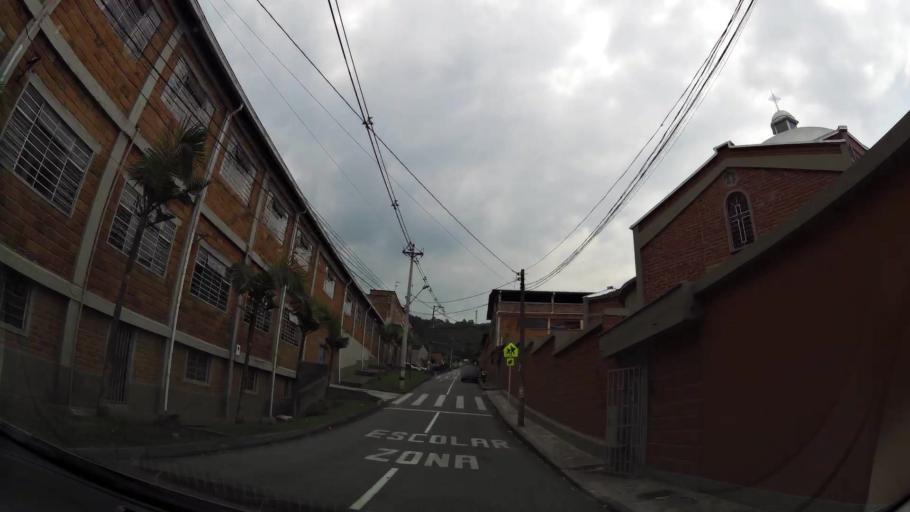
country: CO
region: Antioquia
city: Medellin
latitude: 6.2325
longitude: -75.5488
